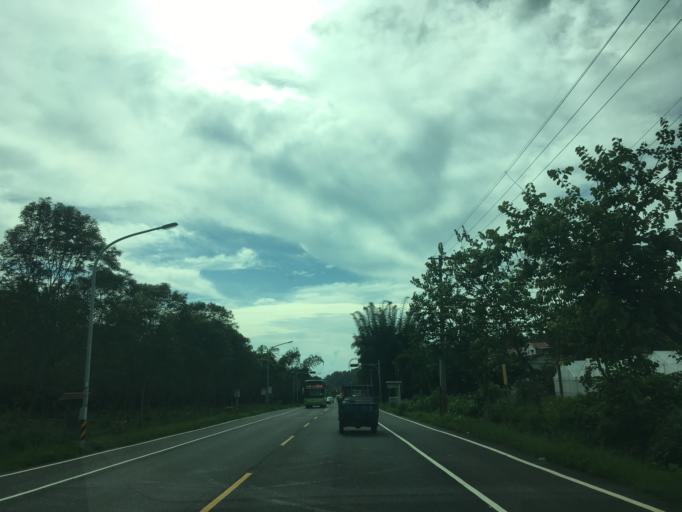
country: TW
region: Taiwan
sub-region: Chiayi
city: Jiayi Shi
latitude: 23.4498
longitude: 120.5721
